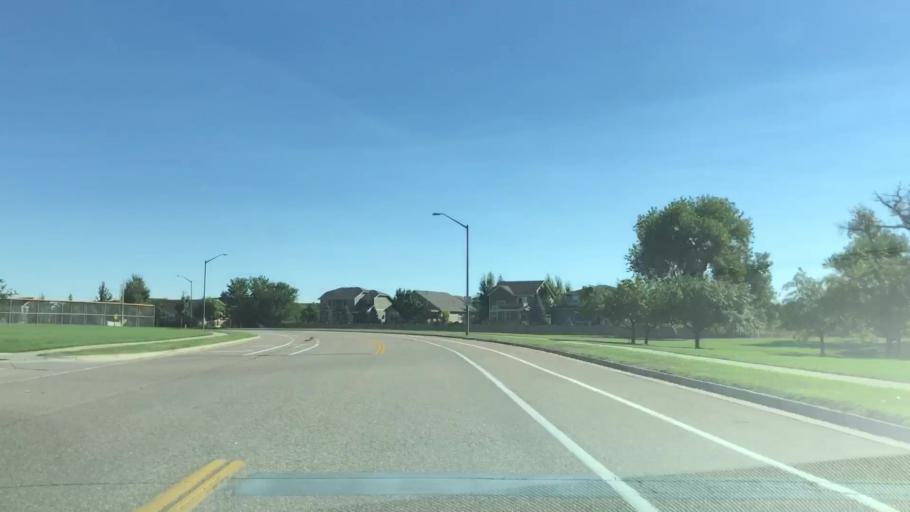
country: US
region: Colorado
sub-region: Larimer County
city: Fort Collins
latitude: 40.5106
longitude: -105.0120
